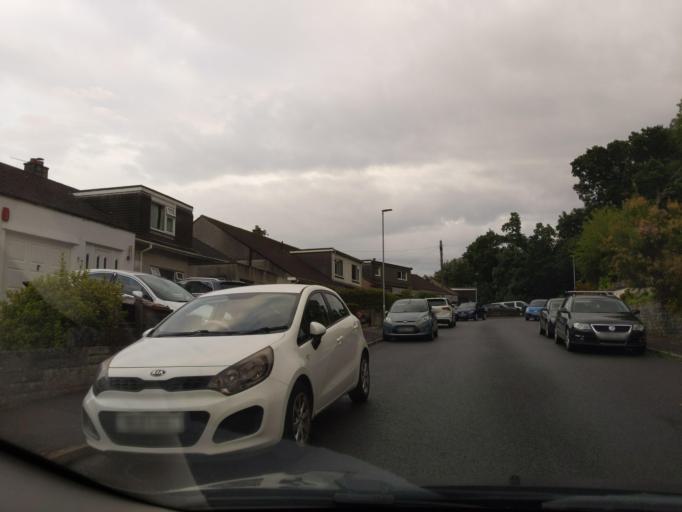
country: GB
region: England
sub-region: Devon
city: Plympton
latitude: 50.3844
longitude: -4.0557
